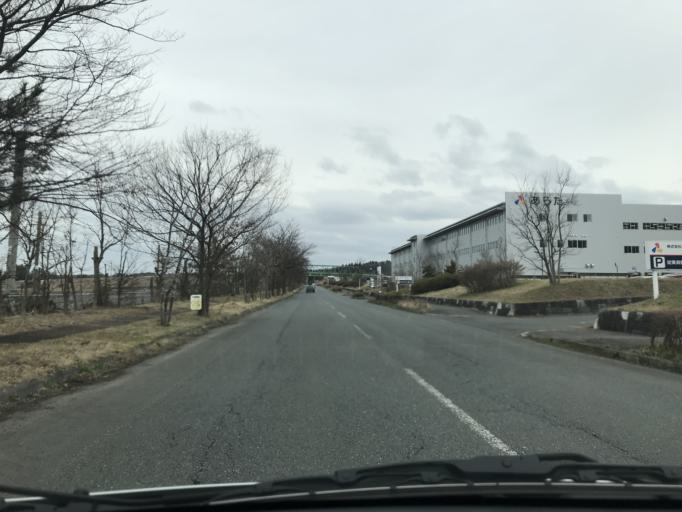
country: JP
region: Iwate
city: Kitakami
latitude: 39.2528
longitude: 141.1045
